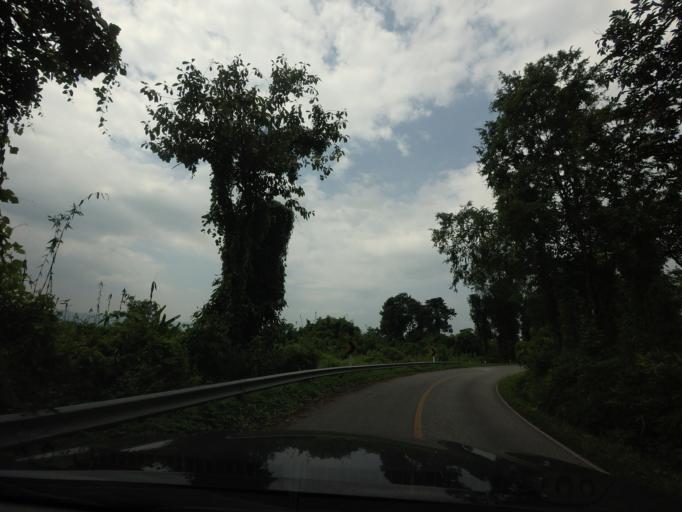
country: TH
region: Uttaradit
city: Nam Pat
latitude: 17.7286
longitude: 100.9472
